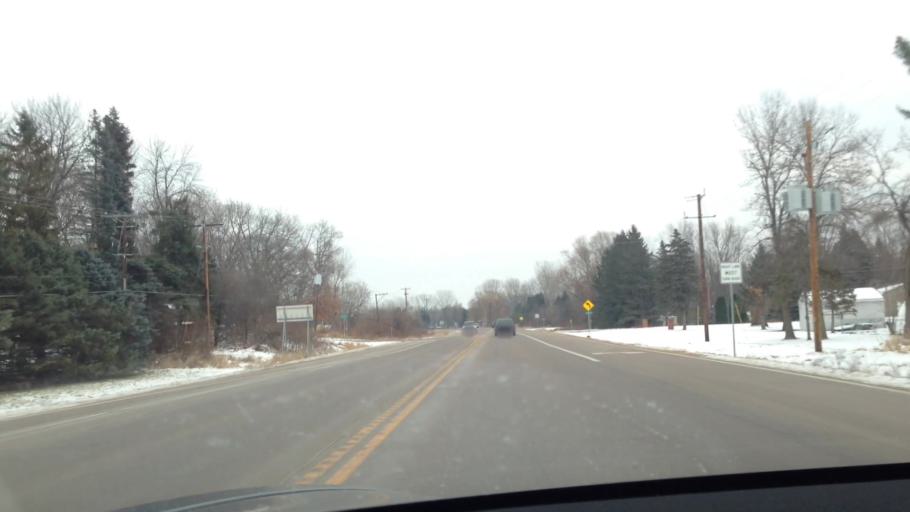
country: US
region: Minnesota
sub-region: Washington County
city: Forest Lake
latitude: 45.2609
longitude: -92.9570
